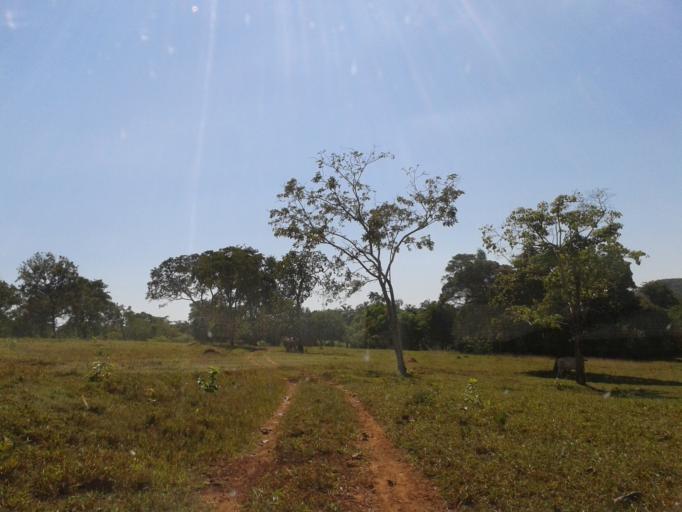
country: BR
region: Minas Gerais
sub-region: Campina Verde
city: Campina Verde
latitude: -19.3997
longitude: -49.7431
